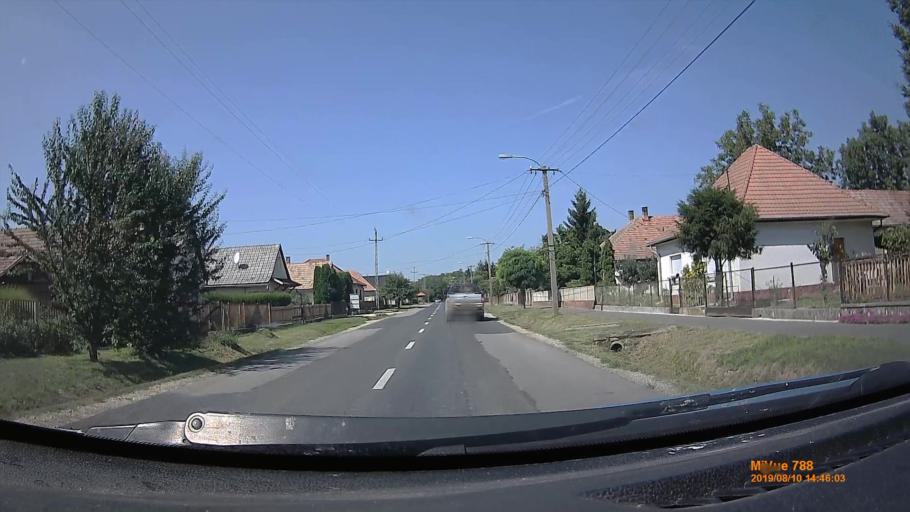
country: HU
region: Somogy
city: Somogyvar
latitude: 46.5889
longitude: 17.6443
